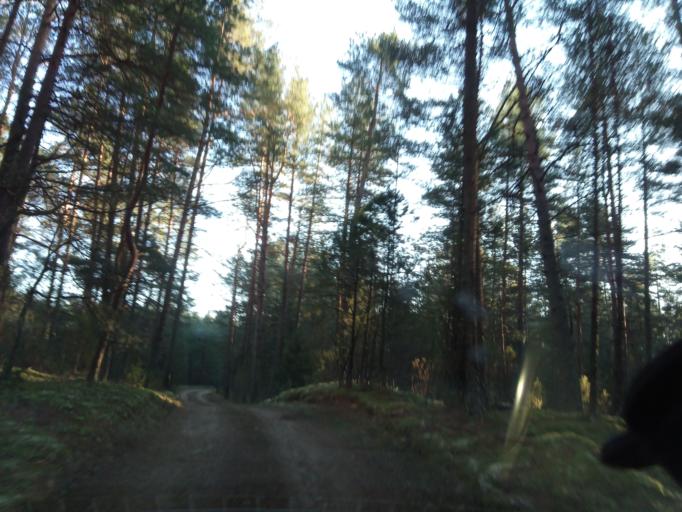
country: LT
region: Alytaus apskritis
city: Druskininkai
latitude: 53.9673
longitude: 23.9697
